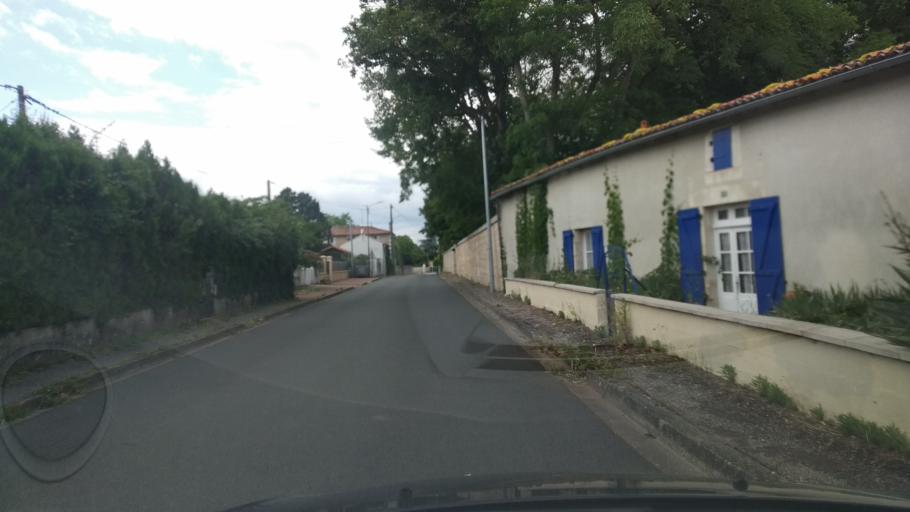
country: FR
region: Poitou-Charentes
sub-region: Departement de la Vienne
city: Vouille
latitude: 46.6309
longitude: 0.1848
